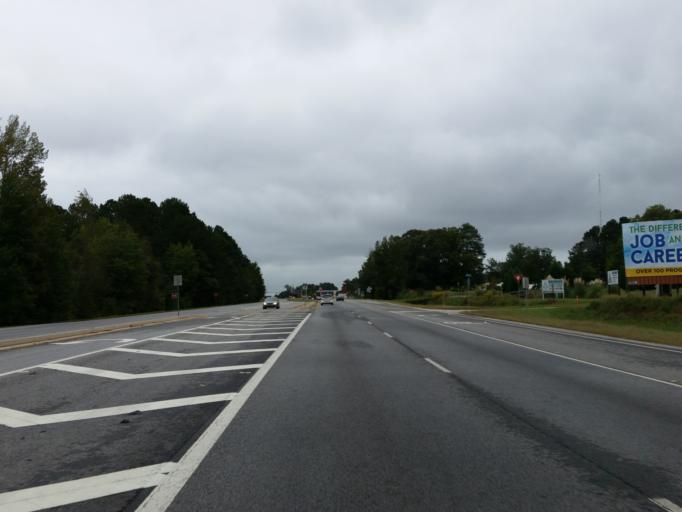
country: US
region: Georgia
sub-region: Henry County
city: Hampton
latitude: 33.3544
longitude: -84.2963
